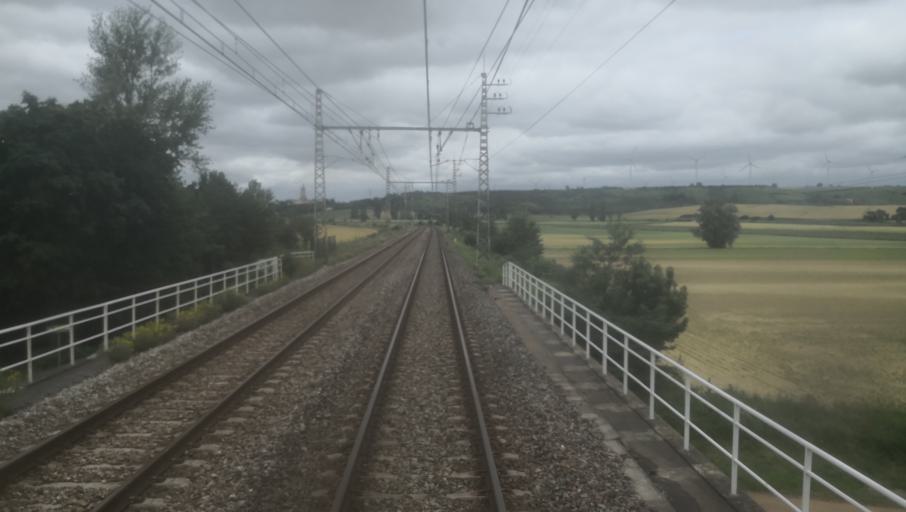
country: FR
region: Midi-Pyrenees
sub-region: Departement de la Haute-Garonne
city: Avignonet-Lauragais
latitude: 43.3572
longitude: 1.8062
